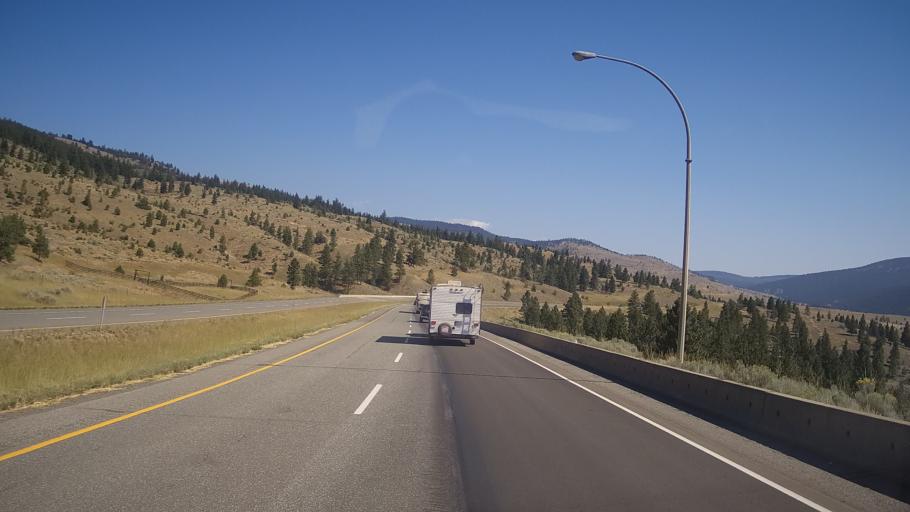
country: CA
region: British Columbia
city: Merritt
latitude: 50.1652
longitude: -120.7068
